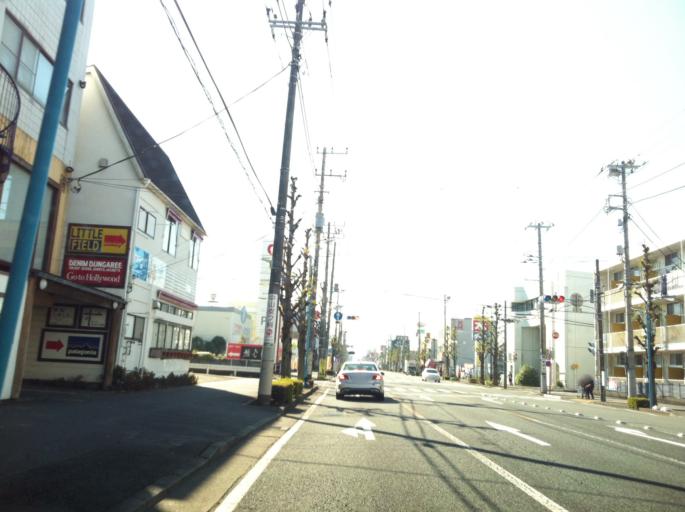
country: JP
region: Shizuoka
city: Numazu
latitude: 35.1185
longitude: 138.8602
